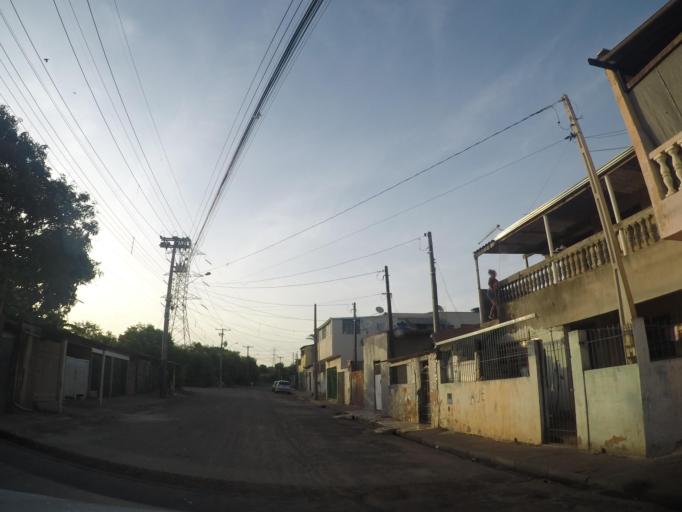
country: BR
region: Sao Paulo
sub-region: Hortolandia
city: Hortolandia
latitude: -22.8516
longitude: -47.1676
